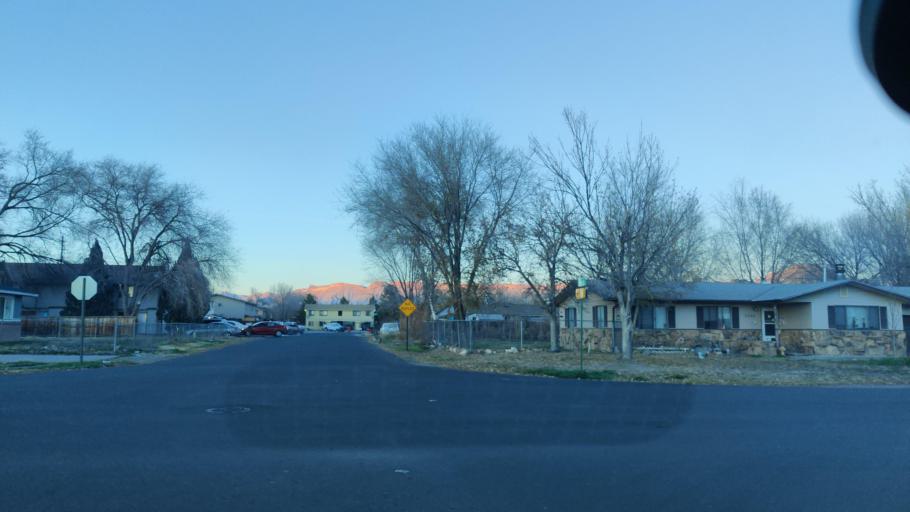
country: US
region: Colorado
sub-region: Mesa County
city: Clifton
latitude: 39.0737
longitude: -108.4587
